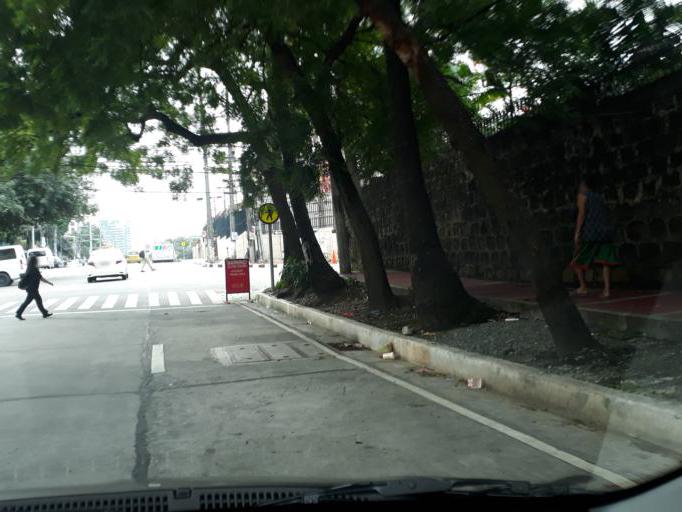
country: PH
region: Metro Manila
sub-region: Quezon City
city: Quezon City
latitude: 14.6413
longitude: 121.0366
